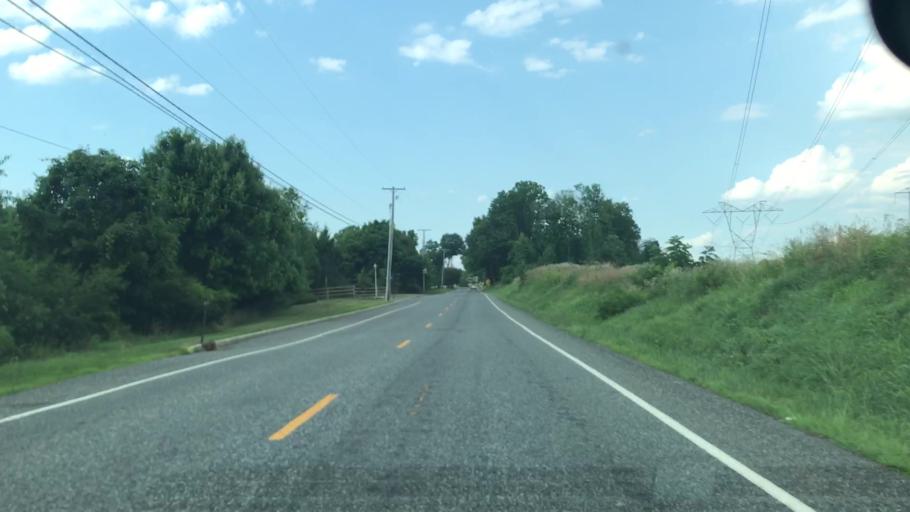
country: US
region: New Jersey
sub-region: Hunterdon County
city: Flemington
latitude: 40.4954
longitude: -74.8095
